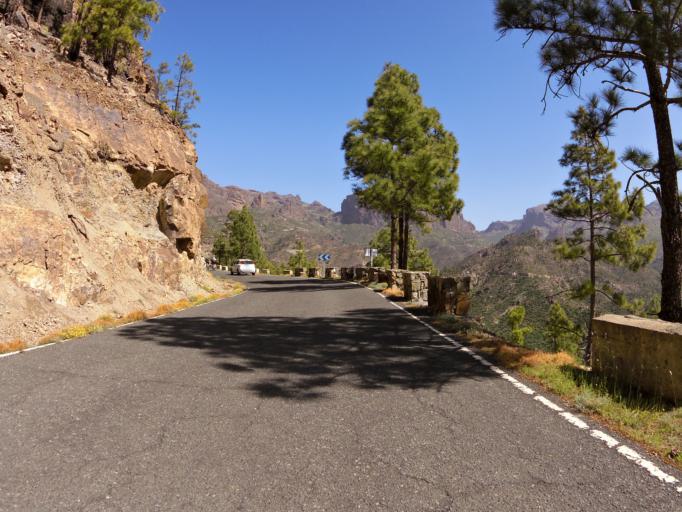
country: ES
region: Canary Islands
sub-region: Provincia de Las Palmas
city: Tejeda
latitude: 27.9403
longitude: -15.6348
